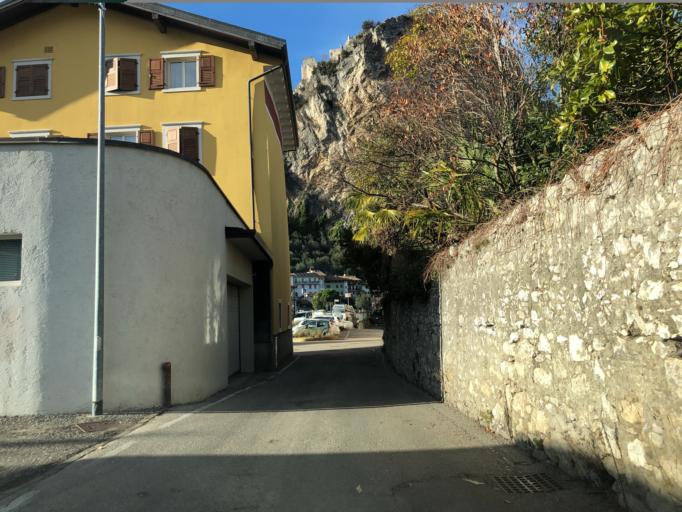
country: IT
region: Trentino-Alto Adige
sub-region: Provincia di Trento
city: Arco
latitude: 45.9200
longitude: 10.8920
